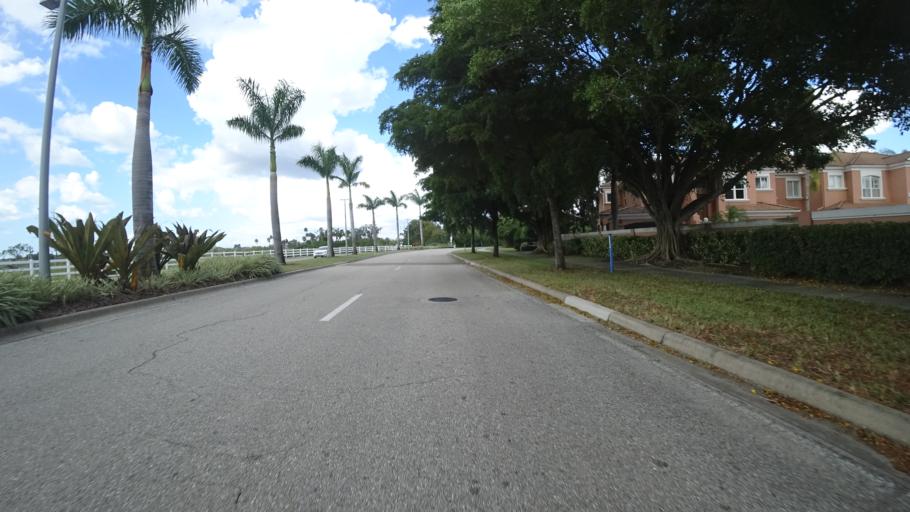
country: US
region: Florida
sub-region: Manatee County
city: Bayshore Gardens
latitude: 27.4453
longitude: -82.6081
